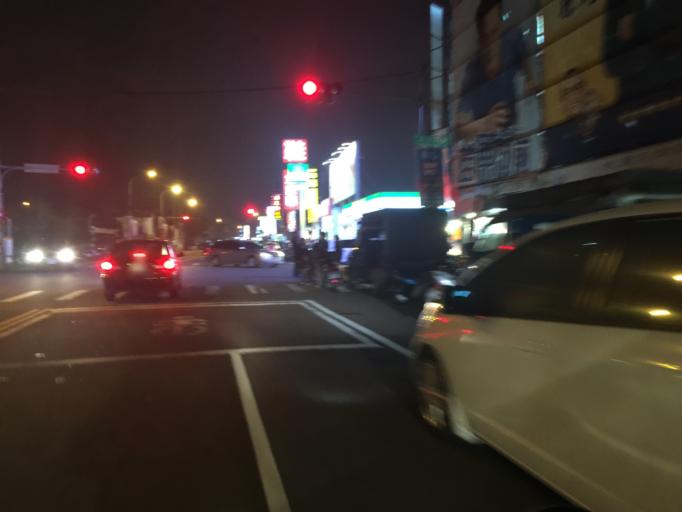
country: TW
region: Taiwan
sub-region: Miaoli
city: Miaoli
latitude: 24.5698
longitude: 120.8209
